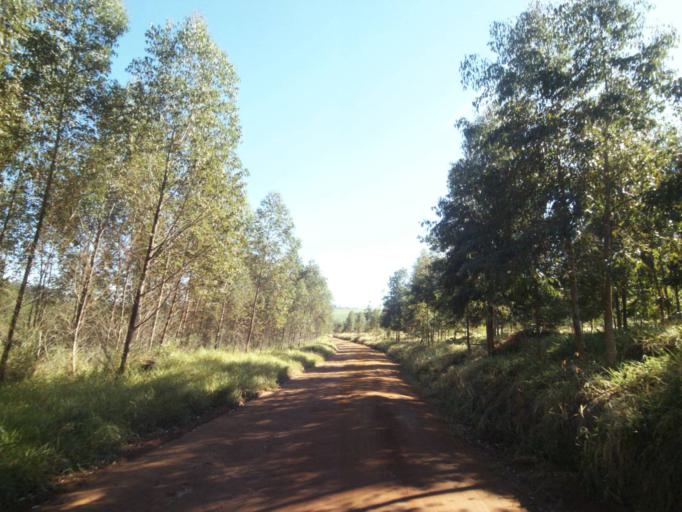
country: BR
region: Parana
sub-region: Tibagi
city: Tibagi
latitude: -24.5399
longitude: -50.3682
